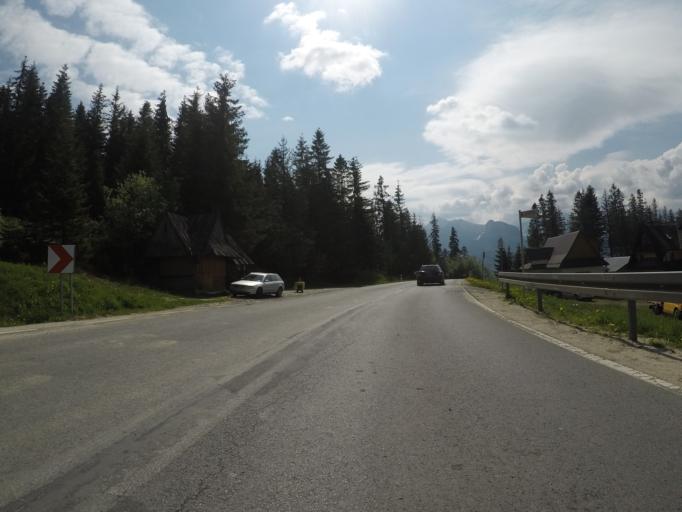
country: PL
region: Lesser Poland Voivodeship
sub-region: Powiat tatrzanski
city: Bukowina Tatrzanska
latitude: 49.3016
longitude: 20.1175
